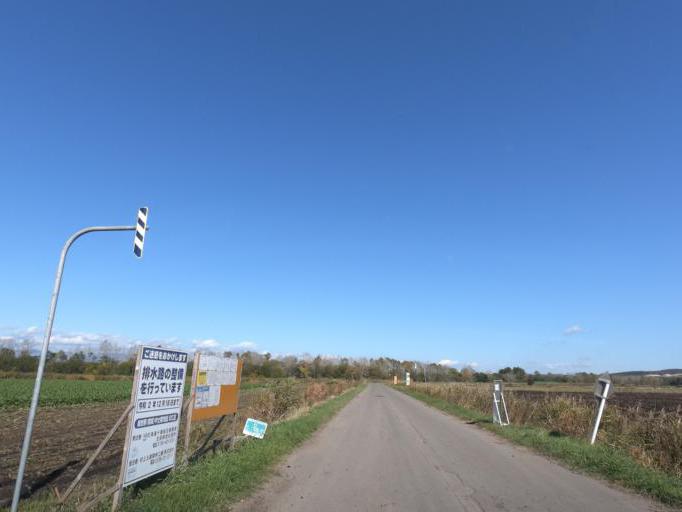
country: JP
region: Hokkaido
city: Otofuke
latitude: 43.0547
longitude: 143.2758
